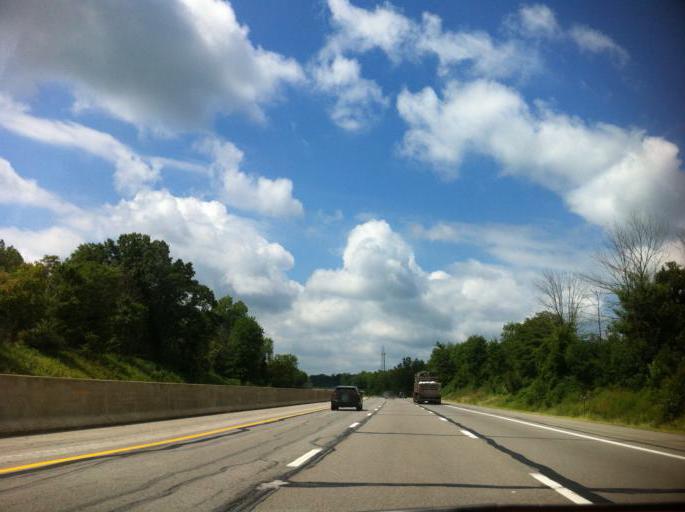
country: US
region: Ohio
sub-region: Lorain County
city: Vermilion
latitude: 41.3448
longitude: -82.3370
